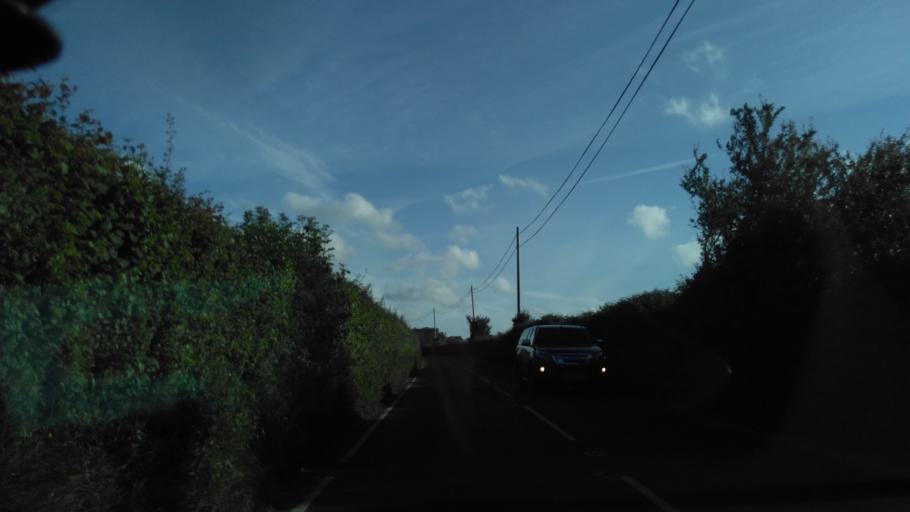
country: GB
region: England
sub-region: Kent
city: Kennington
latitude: 51.2365
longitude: 0.8738
